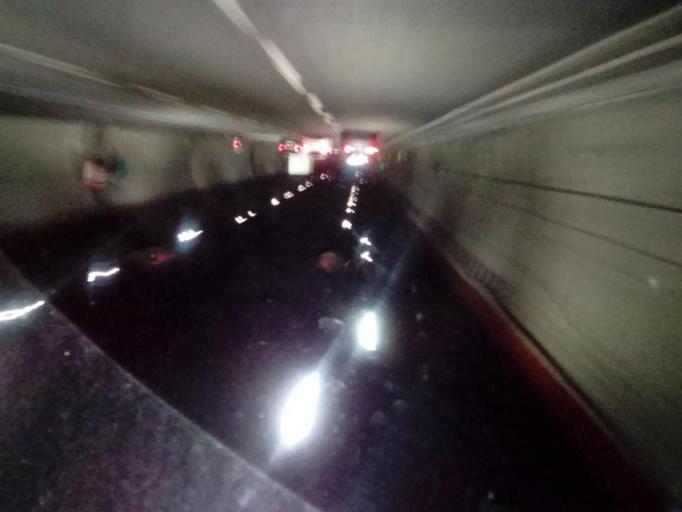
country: IT
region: Latium
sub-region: Citta metropolitana di Roma Capitale
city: Borgo Lotti
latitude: 41.8063
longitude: 12.5621
